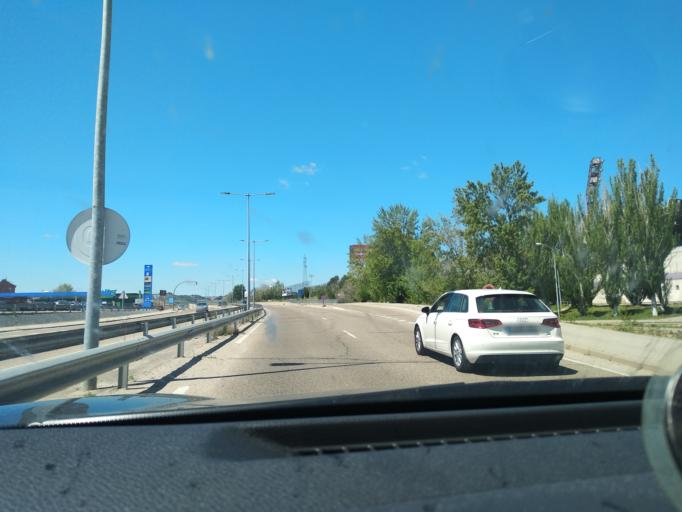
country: ES
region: Castille and Leon
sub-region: Provincia de Valladolid
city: Zaratan
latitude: 41.6432
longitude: -4.7608
